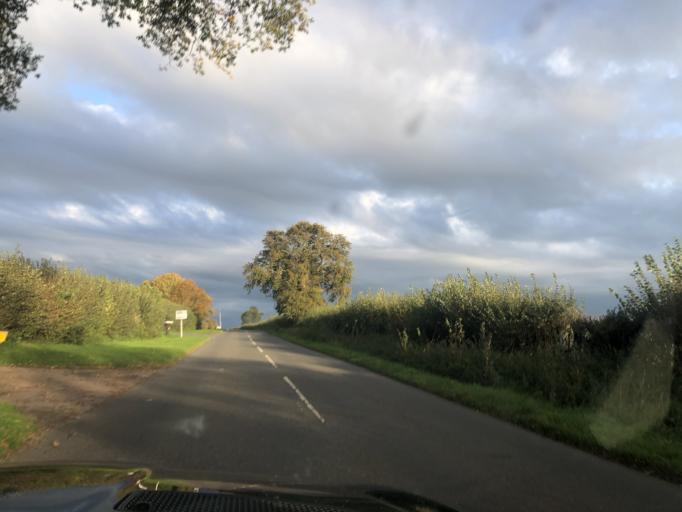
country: GB
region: England
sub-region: Warwickshire
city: Harbury
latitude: 52.2336
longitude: -1.4779
